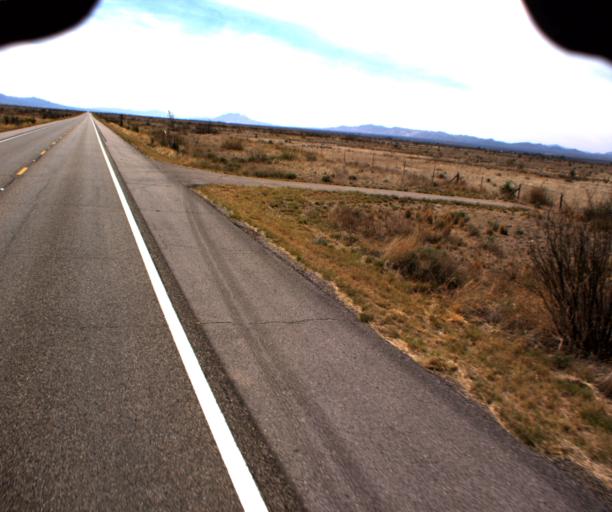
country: US
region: Arizona
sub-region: Cochise County
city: Pirtleville
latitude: 31.4850
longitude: -109.6269
